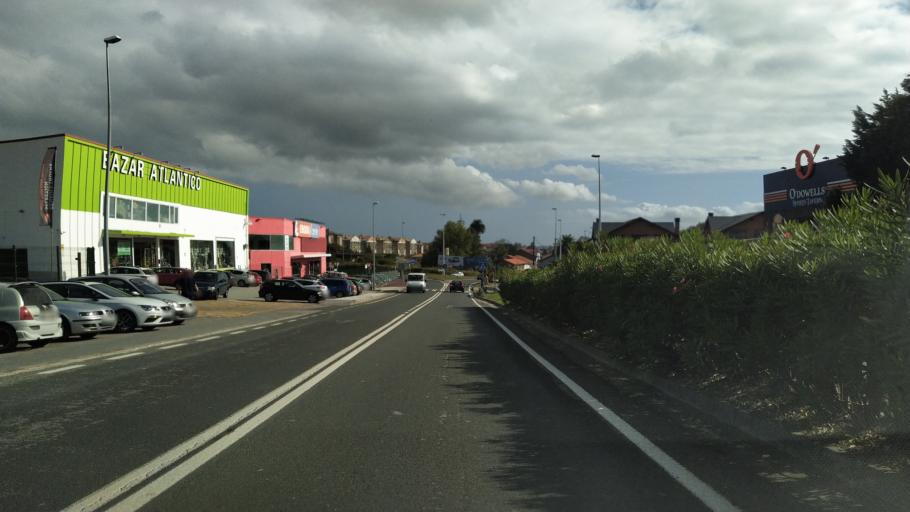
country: ES
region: Cantabria
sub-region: Provincia de Cantabria
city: Santa Cruz de Bezana
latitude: 43.4356
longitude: -3.9085
